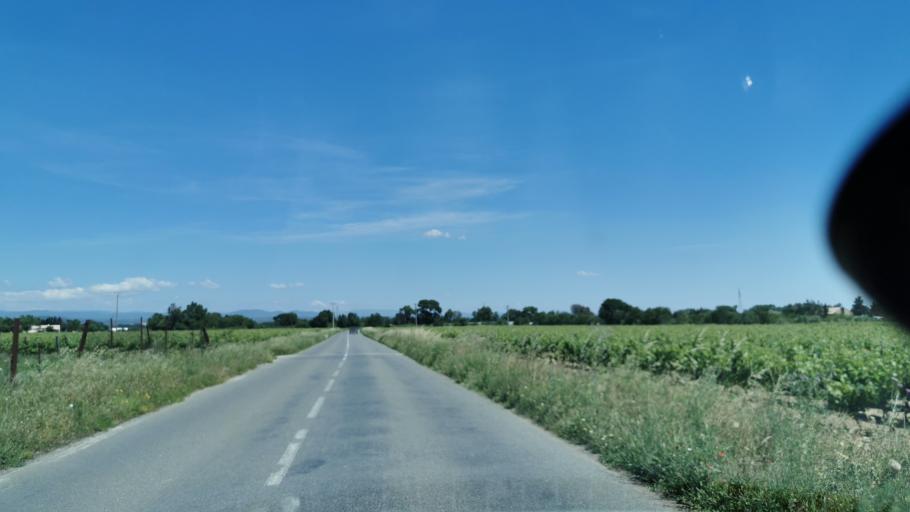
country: FR
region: Languedoc-Roussillon
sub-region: Departement de l'Aude
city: Saint-Marcel-sur-Aude
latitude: 43.2491
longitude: 2.9291
